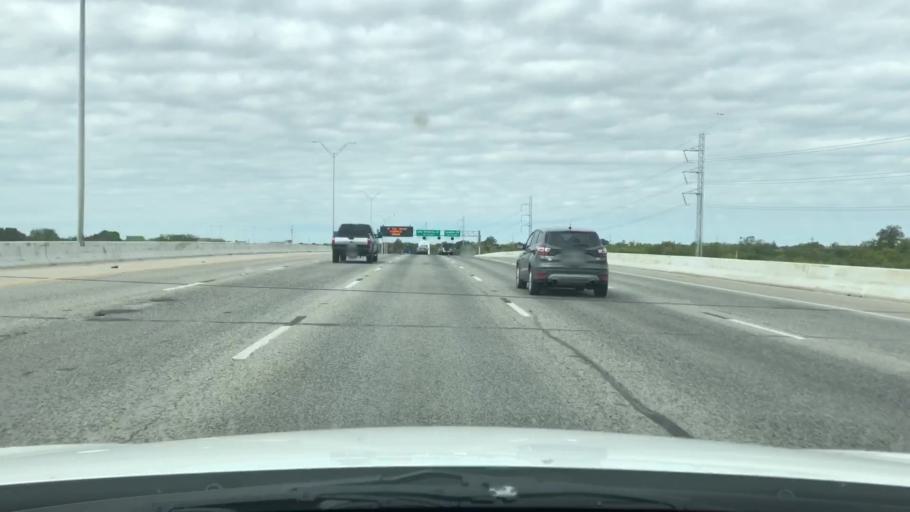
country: US
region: Texas
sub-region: Bexar County
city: San Antonio
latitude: 29.4012
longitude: -98.5365
